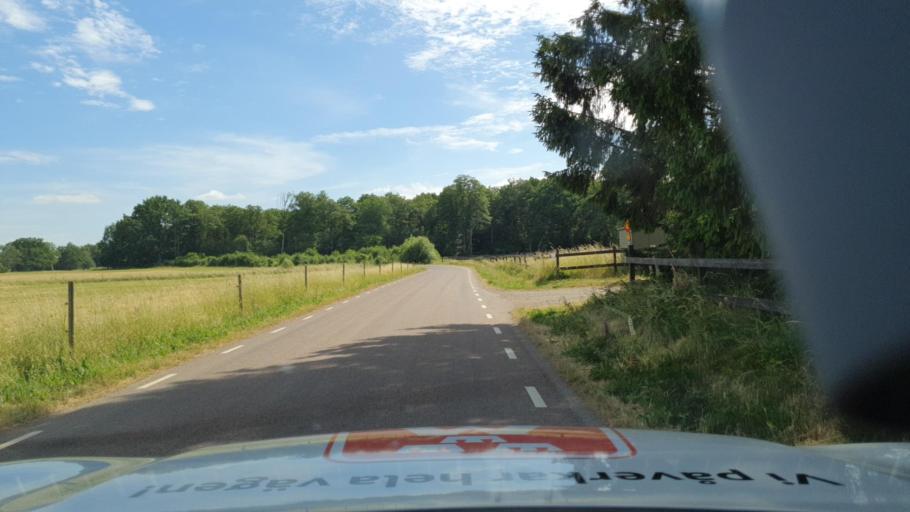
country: SE
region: Skane
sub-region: Sjobo Kommun
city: Blentarp
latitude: 55.6140
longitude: 13.6183
